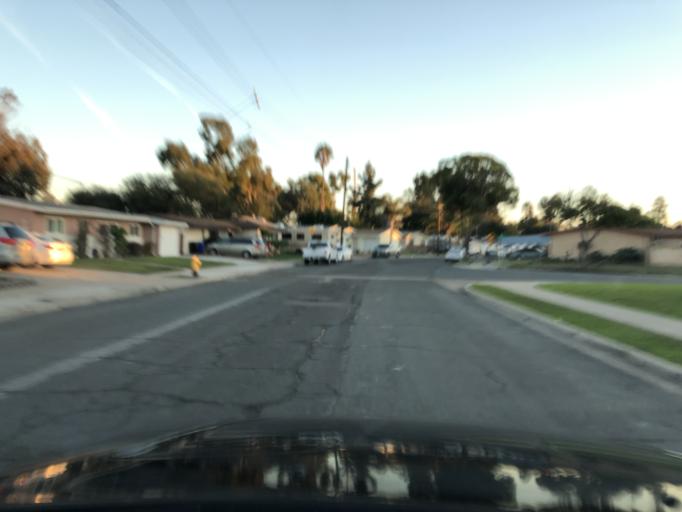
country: US
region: California
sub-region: San Diego County
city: La Jolla
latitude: 32.8363
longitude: -117.1725
